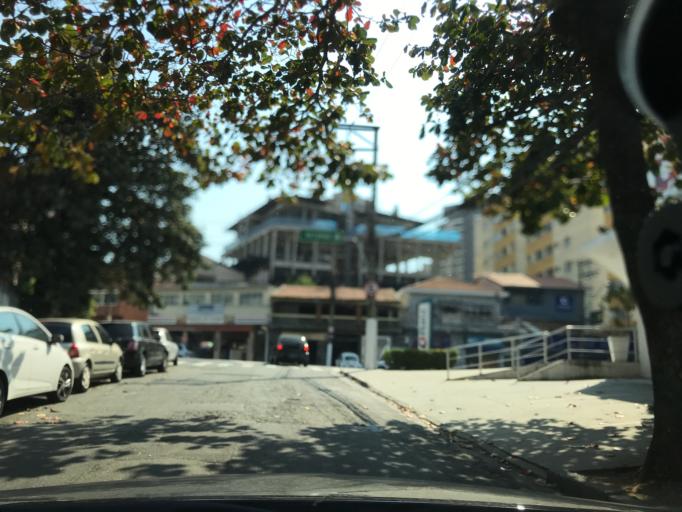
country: BR
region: Sao Paulo
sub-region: Osasco
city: Osasco
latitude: -23.5431
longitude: -46.7734
